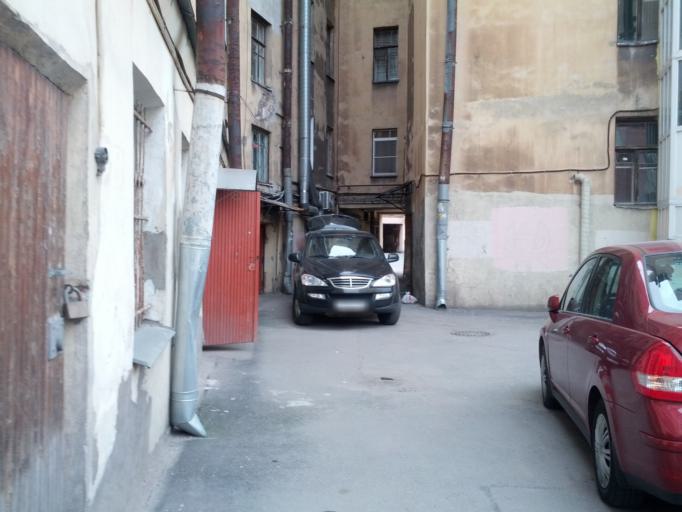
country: RU
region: St.-Petersburg
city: Centralniy
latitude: 59.9183
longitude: 30.3472
